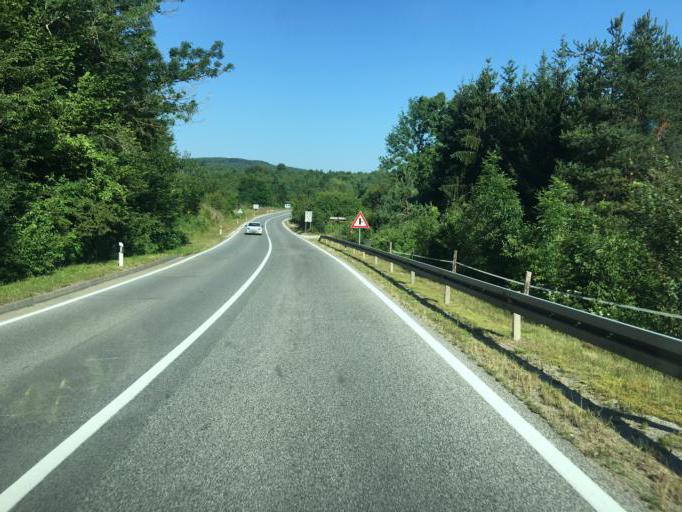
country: HR
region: Karlovacka
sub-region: Grad Karlovac
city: Slunj
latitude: 45.0567
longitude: 15.6235
